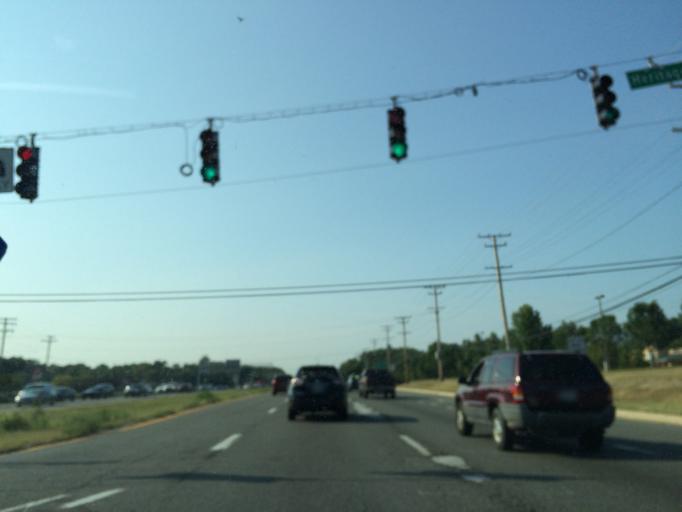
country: US
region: Maryland
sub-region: Prince George's County
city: Bowie
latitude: 38.9457
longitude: -76.7181
